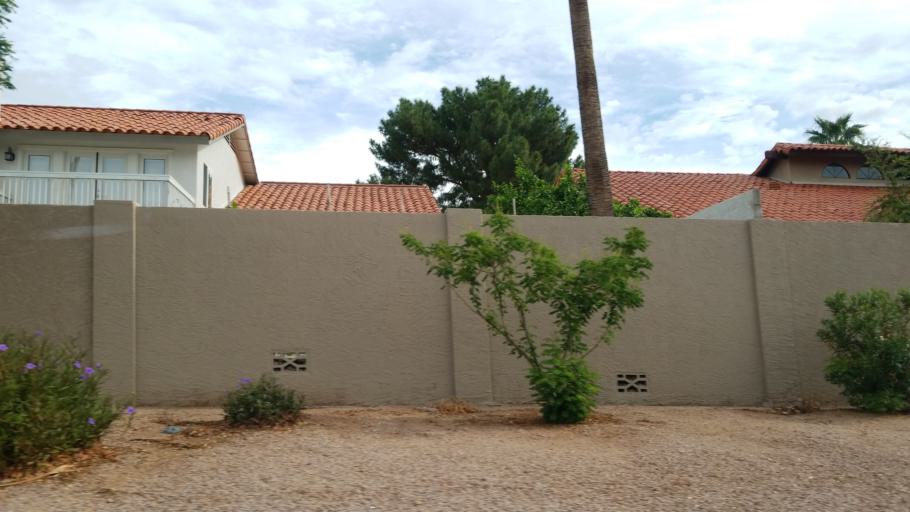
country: US
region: Arizona
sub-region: Maricopa County
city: Paradise Valley
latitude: 33.5745
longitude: -111.9009
